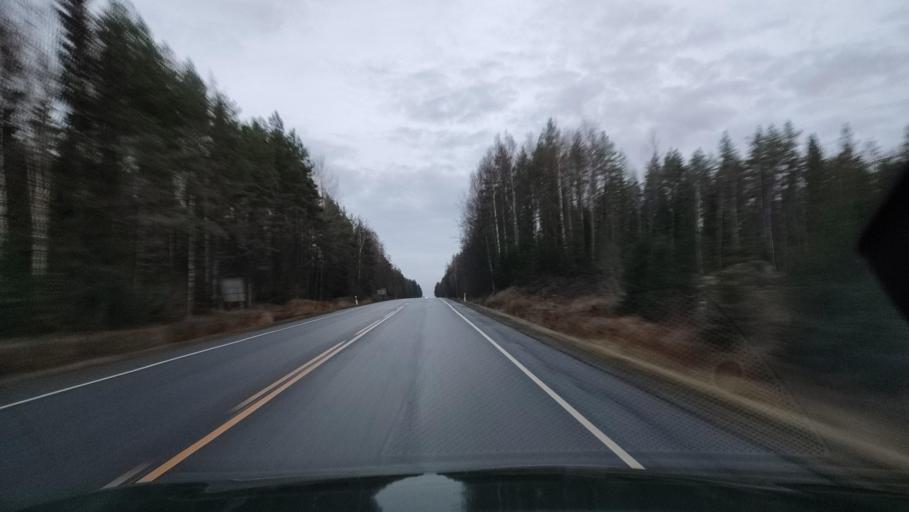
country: FI
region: Ostrobothnia
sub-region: Vaasa
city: Ristinummi
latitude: 62.9691
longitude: 21.7674
